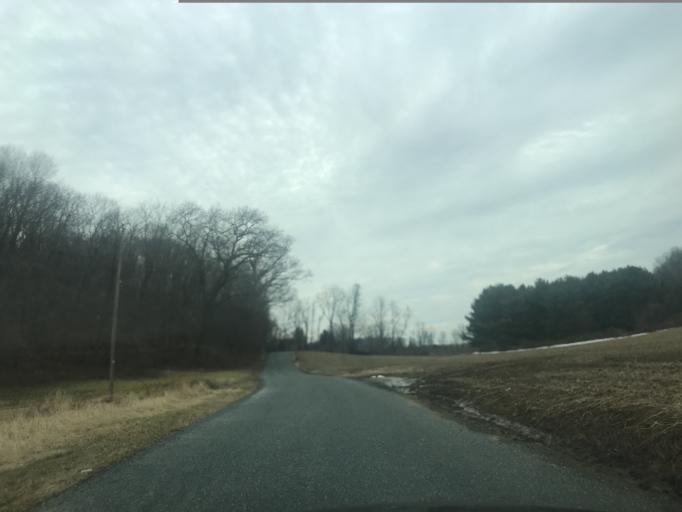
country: US
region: Maryland
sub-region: Harford County
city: Jarrettsville
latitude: 39.6736
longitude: -76.4141
